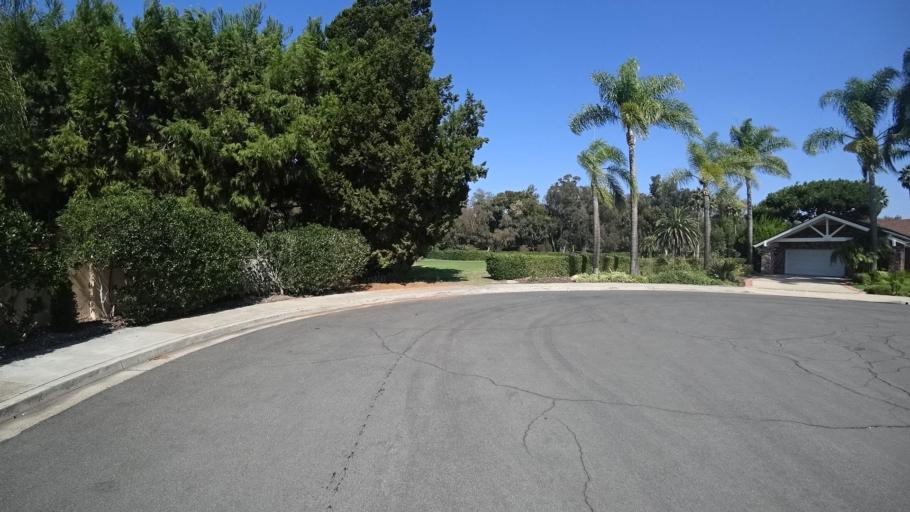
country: US
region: California
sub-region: San Diego County
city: Fairbanks Ranch
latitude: 32.9960
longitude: -117.2077
